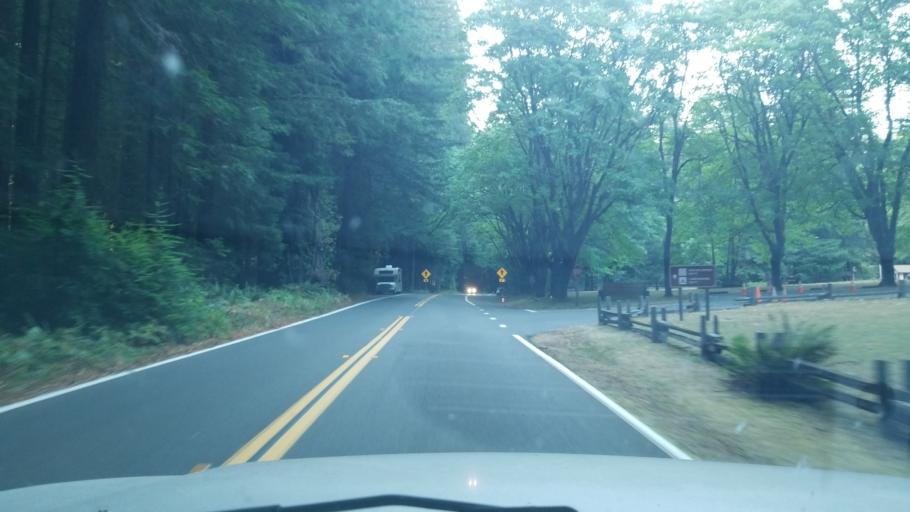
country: US
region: California
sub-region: Humboldt County
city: Redway
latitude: 40.3070
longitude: -123.9074
